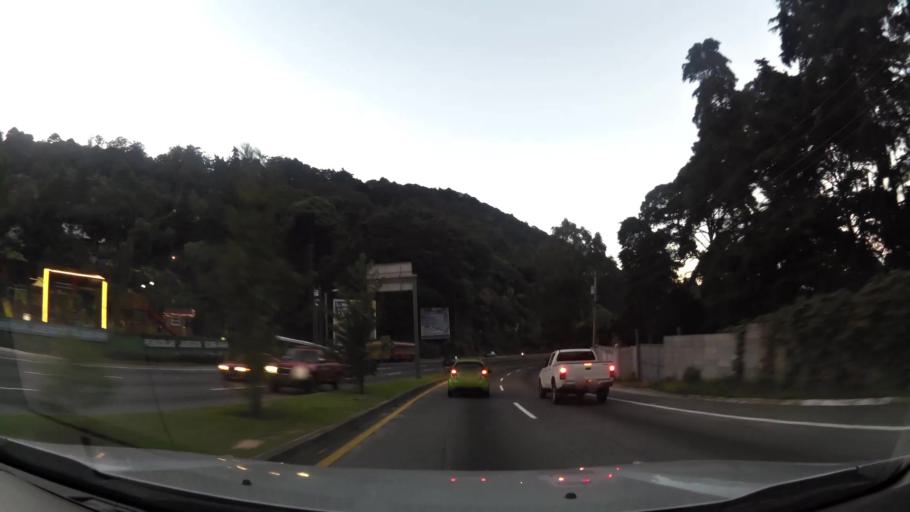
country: GT
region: Guatemala
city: Mixco
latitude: 14.6135
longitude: -90.6221
